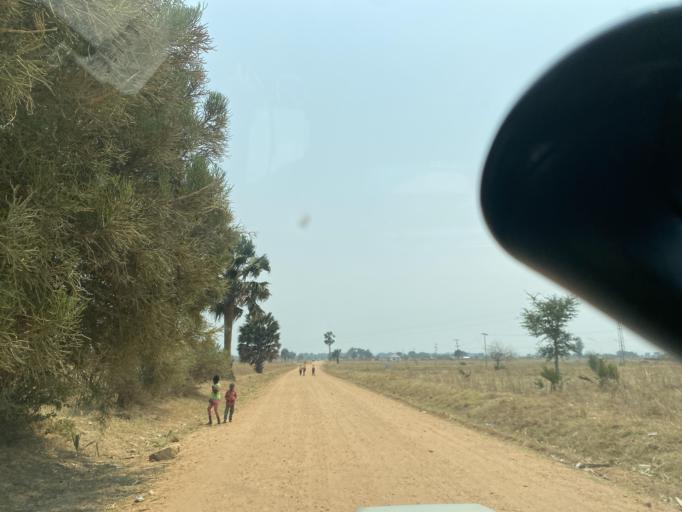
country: ZM
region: Lusaka
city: Kafue
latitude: -15.6402
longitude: 28.0983
